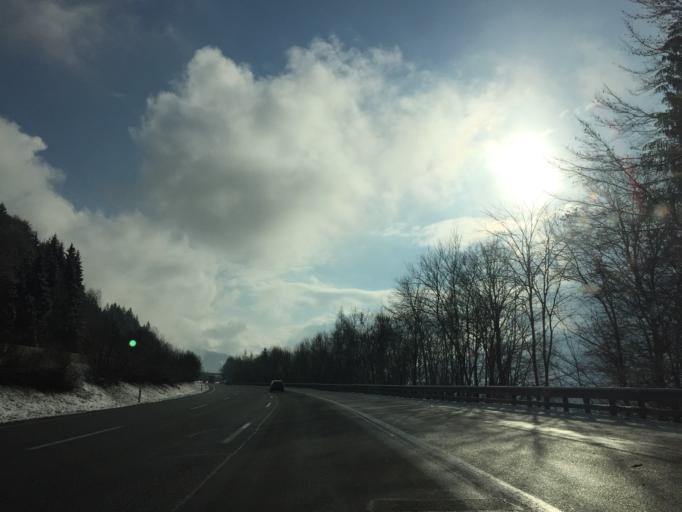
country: AT
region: Salzburg
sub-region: Politischer Bezirk Sankt Johann im Pongau
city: Werfenweng
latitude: 47.4359
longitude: 13.2447
